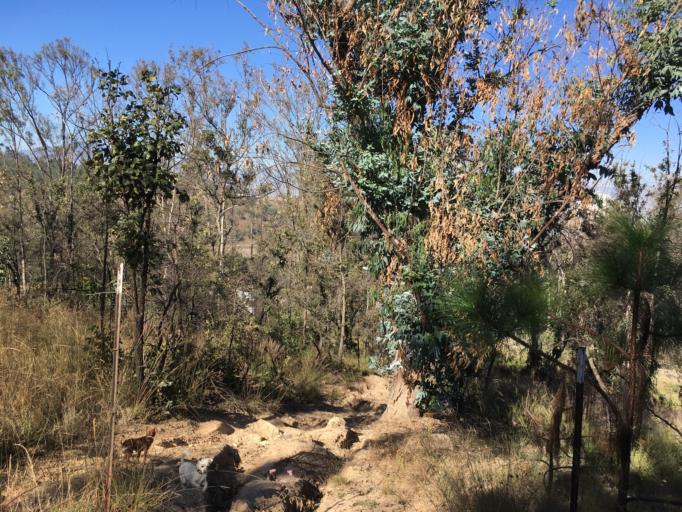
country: MX
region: Michoacan
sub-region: Morelia
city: Montana Monarca (Punta Altozano)
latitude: 19.6694
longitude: -101.1511
